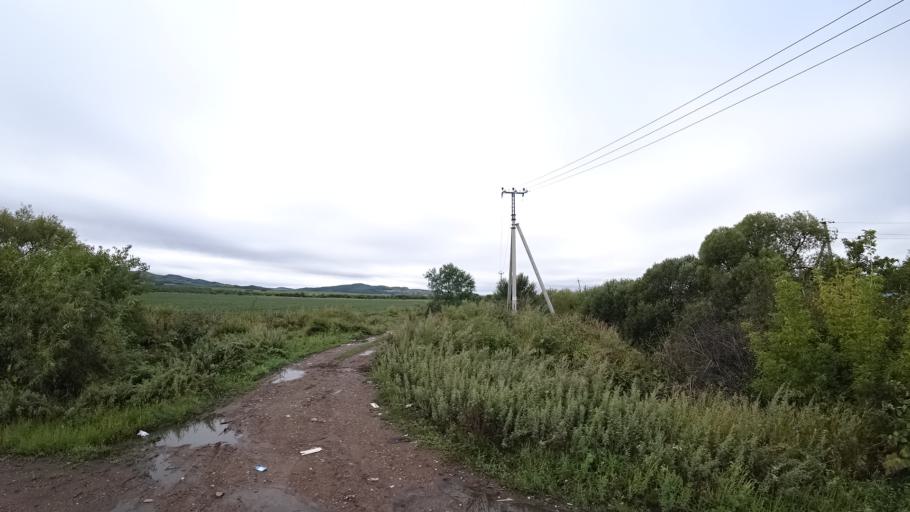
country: RU
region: Primorskiy
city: Monastyrishche
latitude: 44.1838
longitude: 132.4833
